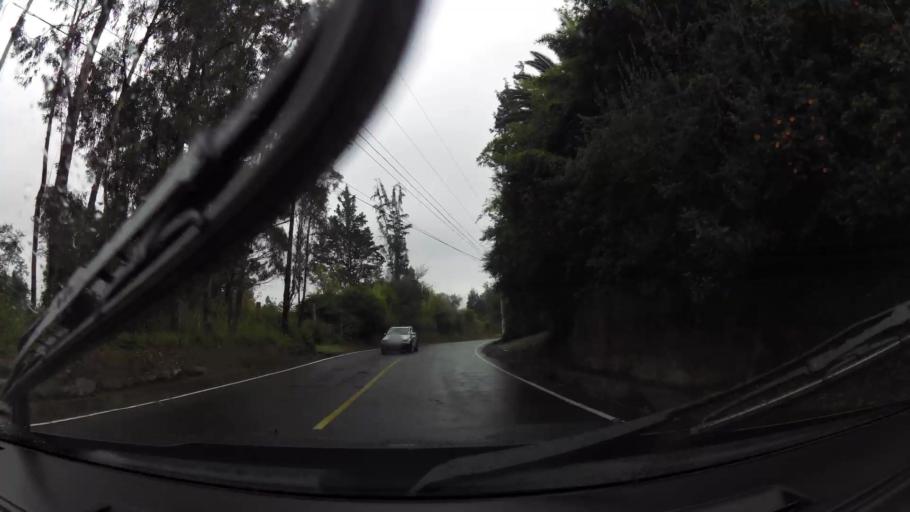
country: EC
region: Pichincha
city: Sangolqui
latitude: -0.2827
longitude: -78.4446
